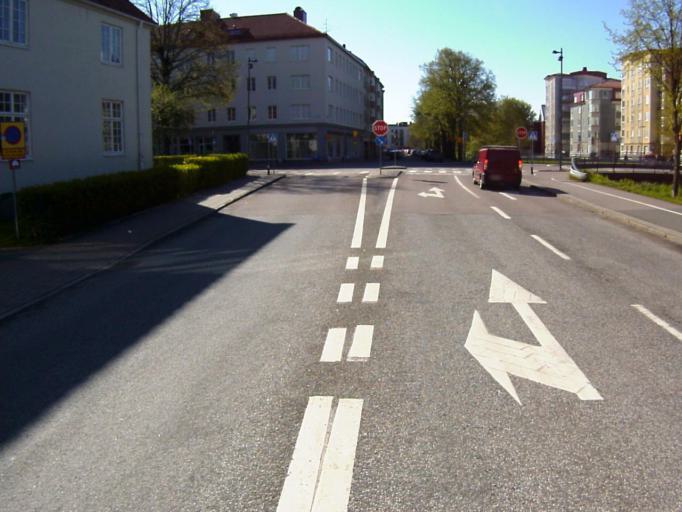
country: SE
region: Skane
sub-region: Kristianstads Kommun
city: Kristianstad
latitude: 56.0297
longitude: 14.1613
